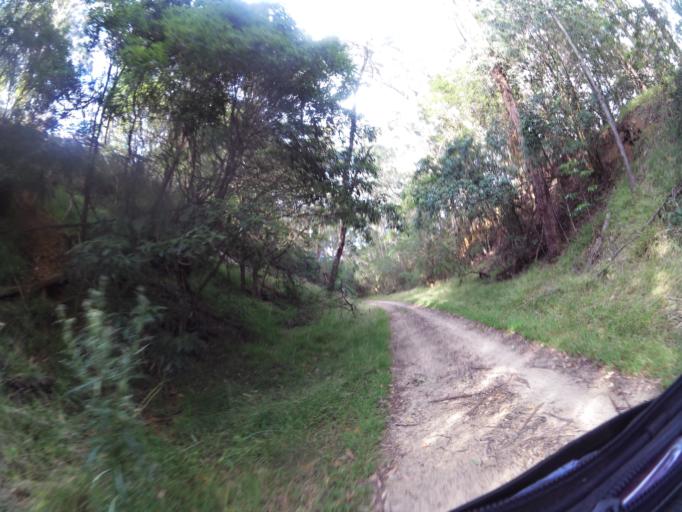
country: AU
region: Victoria
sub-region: East Gippsland
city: Lakes Entrance
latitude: -37.7267
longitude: 148.4263
